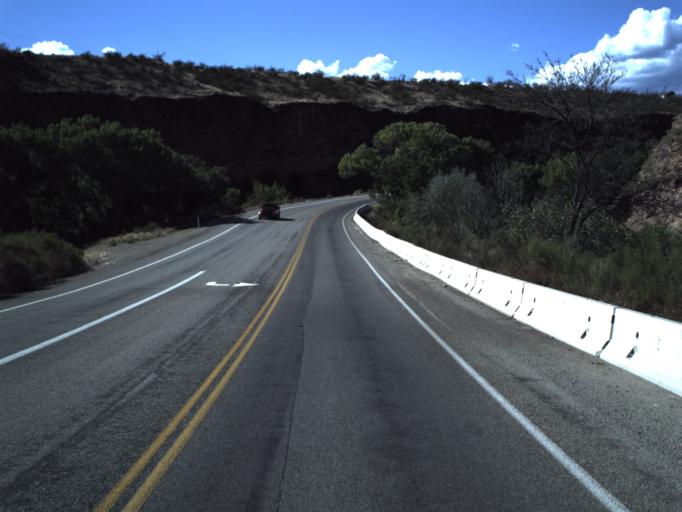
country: US
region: Utah
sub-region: Washington County
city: LaVerkin
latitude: 37.2237
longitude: -113.2803
